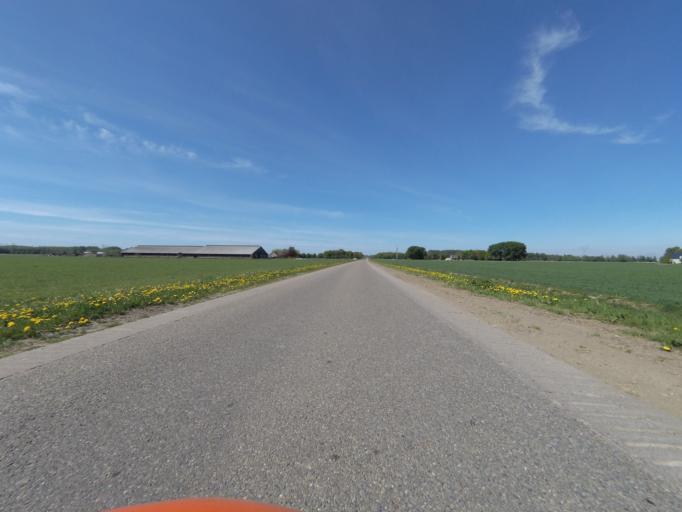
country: NL
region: Flevoland
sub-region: Gemeente Dronten
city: Biddinghuizen
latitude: 52.4152
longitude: 5.6391
